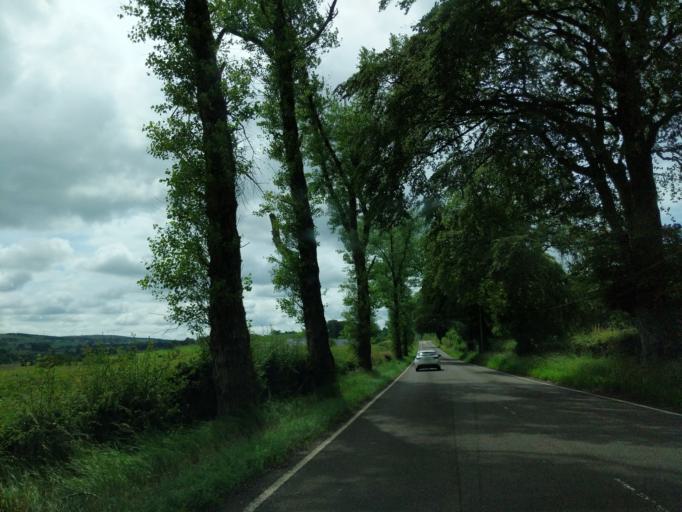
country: GB
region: Scotland
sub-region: South Lanarkshire
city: Strathaven
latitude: 55.6804
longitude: -4.0400
